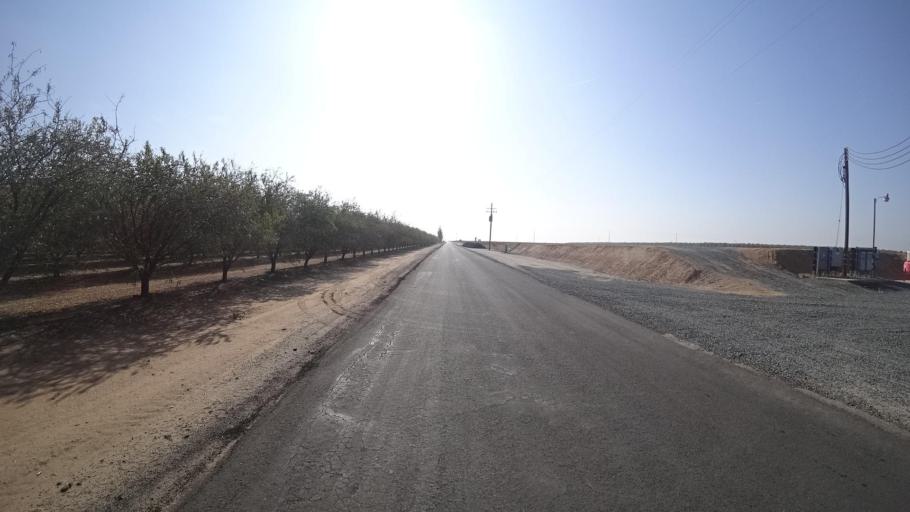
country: US
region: California
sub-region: Kern County
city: McFarland
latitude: 35.6348
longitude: -119.1866
